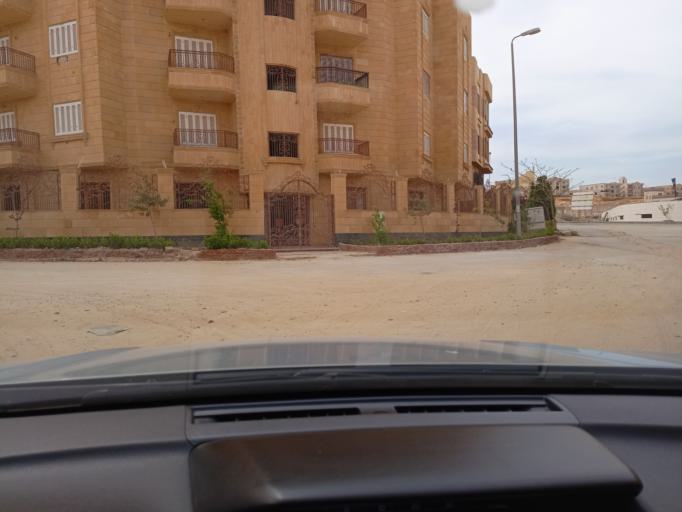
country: EG
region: Muhafazat al Qalyubiyah
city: Al Khankah
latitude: 30.2482
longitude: 31.4980
